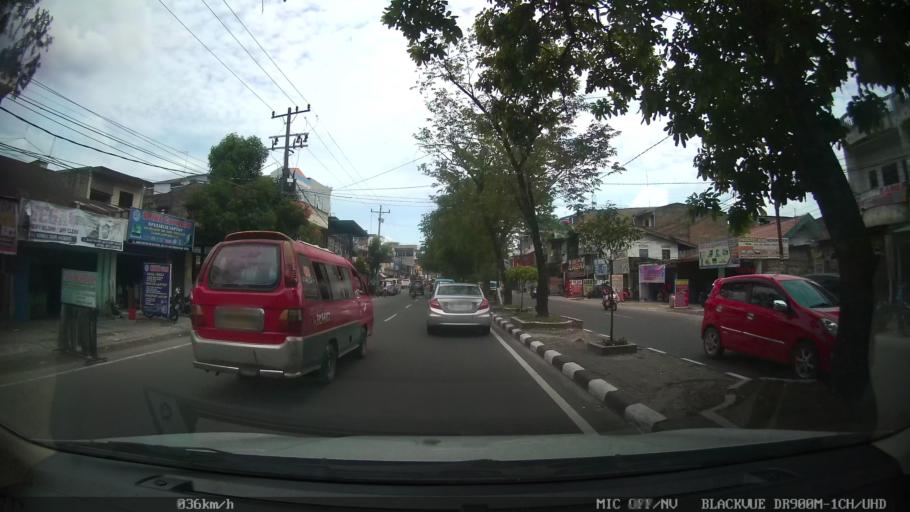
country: ID
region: North Sumatra
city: Medan
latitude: 3.5574
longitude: 98.6618
